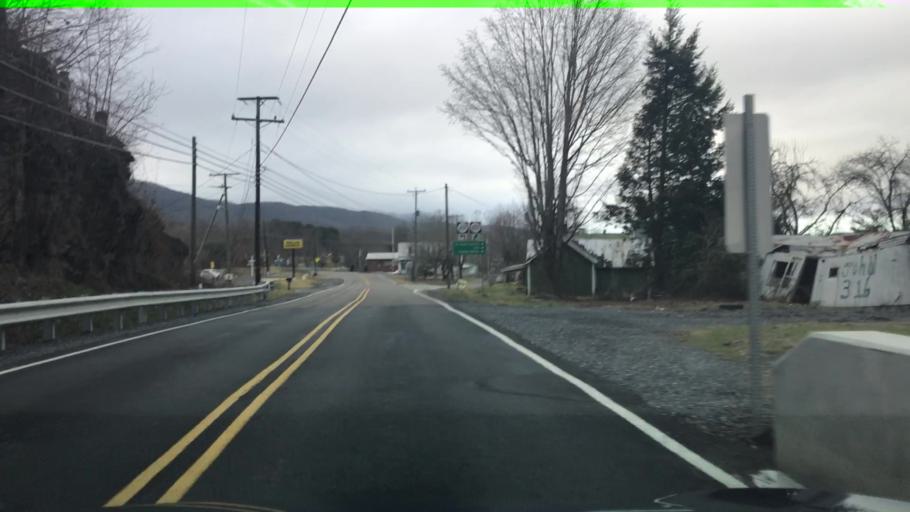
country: US
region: Virginia
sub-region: Smyth County
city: Atkins
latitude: 36.7766
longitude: -81.4111
